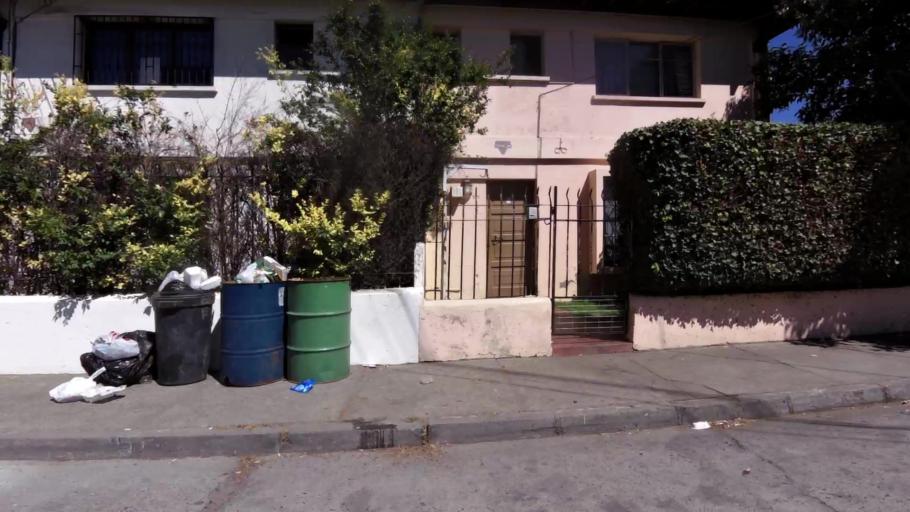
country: CL
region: O'Higgins
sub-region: Provincia de Cachapoal
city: Rancagua
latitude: -34.1732
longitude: -70.7327
